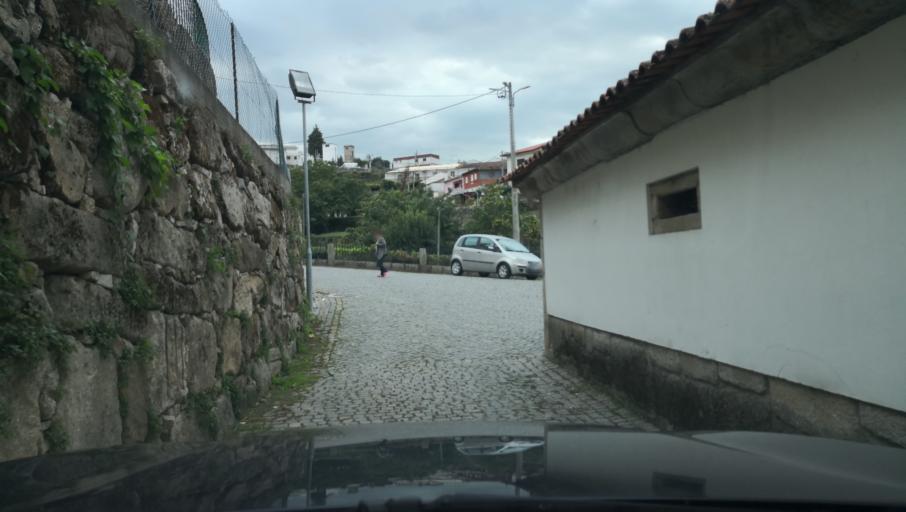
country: PT
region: Vila Real
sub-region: Vila Real
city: Vila Real
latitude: 41.2856
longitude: -7.7621
